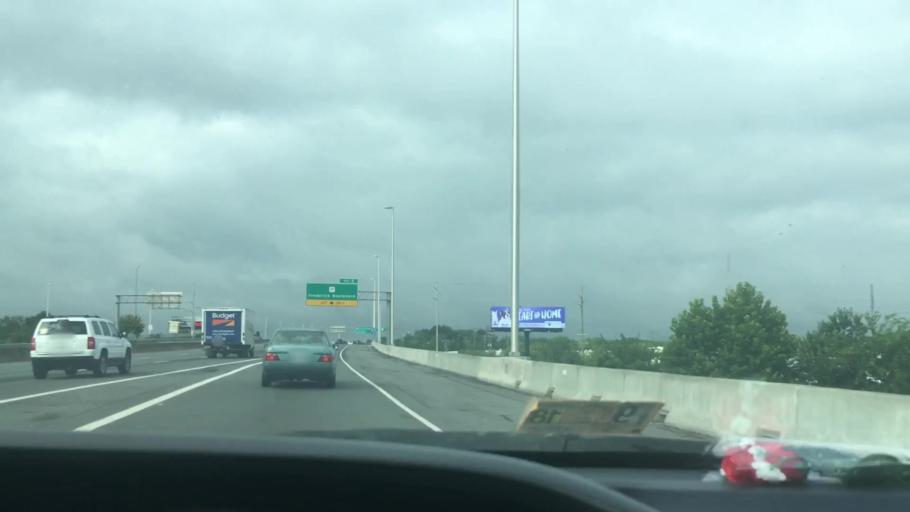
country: US
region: Virginia
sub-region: City of Portsmouth
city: Portsmouth
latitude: 36.8258
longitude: -76.3273
